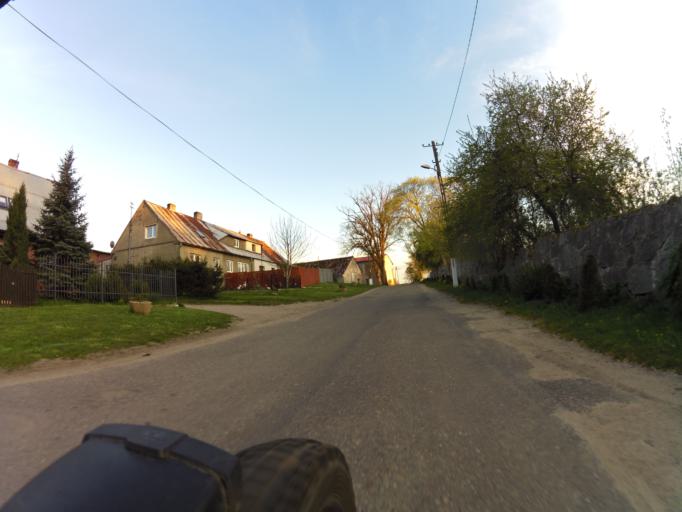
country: PL
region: West Pomeranian Voivodeship
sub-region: Powiat lobeski
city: Lobez
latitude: 53.6975
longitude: 15.6449
